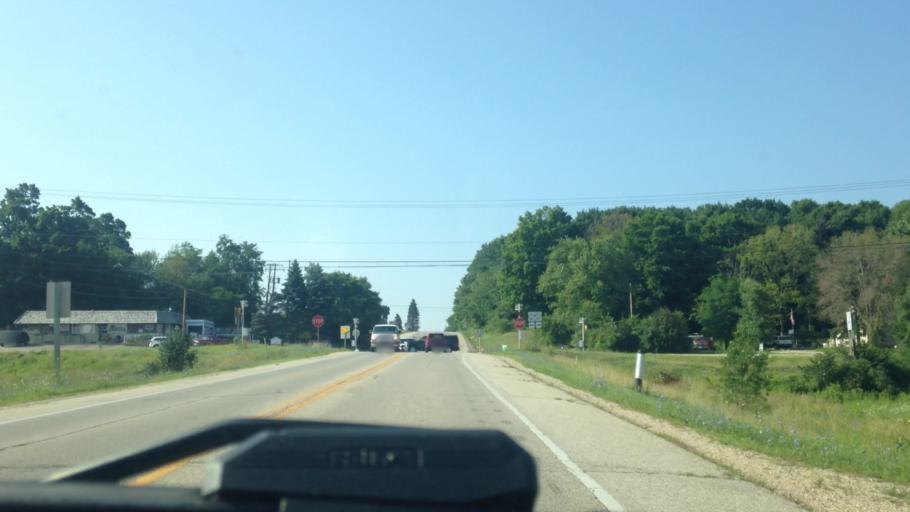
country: US
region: Wisconsin
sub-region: Washington County
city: Richfield
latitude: 43.2522
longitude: -88.2618
